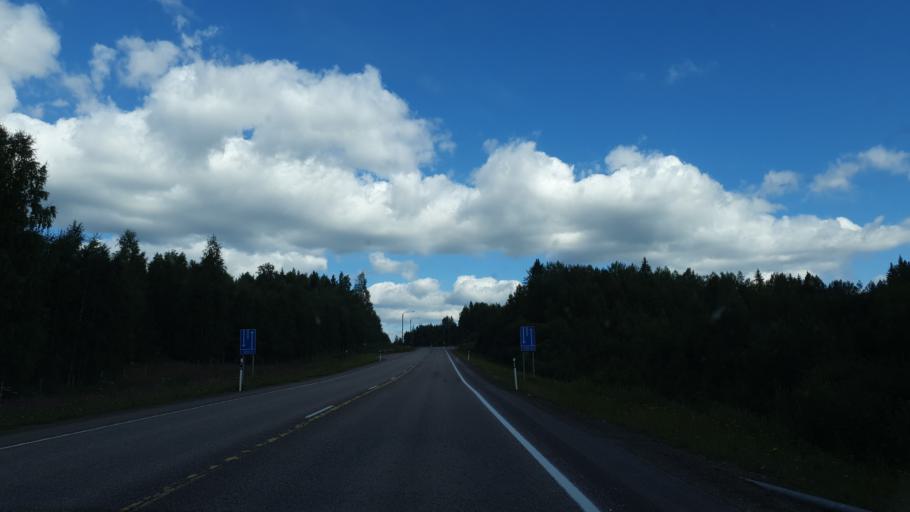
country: FI
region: Central Finland
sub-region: Jaemsae
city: Jaemsae
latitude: 61.8077
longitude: 24.9882
